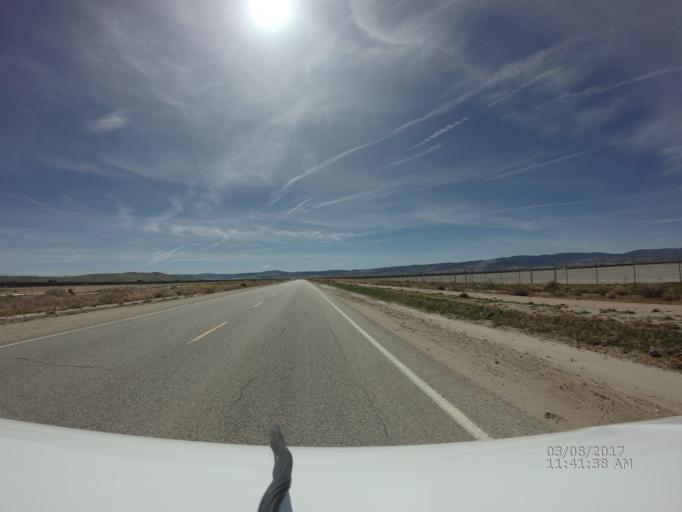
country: US
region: California
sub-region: Los Angeles County
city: Green Valley
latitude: 34.7861
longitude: -118.4315
